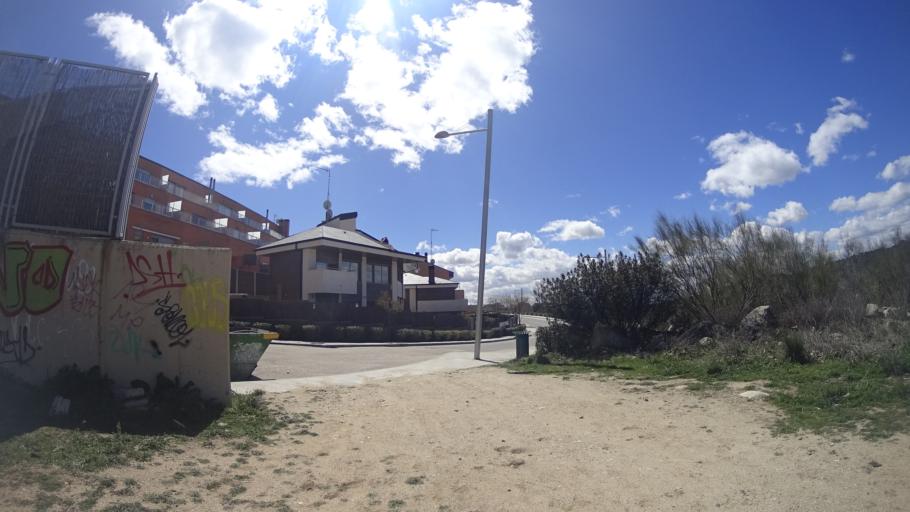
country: ES
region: Madrid
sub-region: Provincia de Madrid
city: Torrelodones
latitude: 40.5663
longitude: -3.9237
